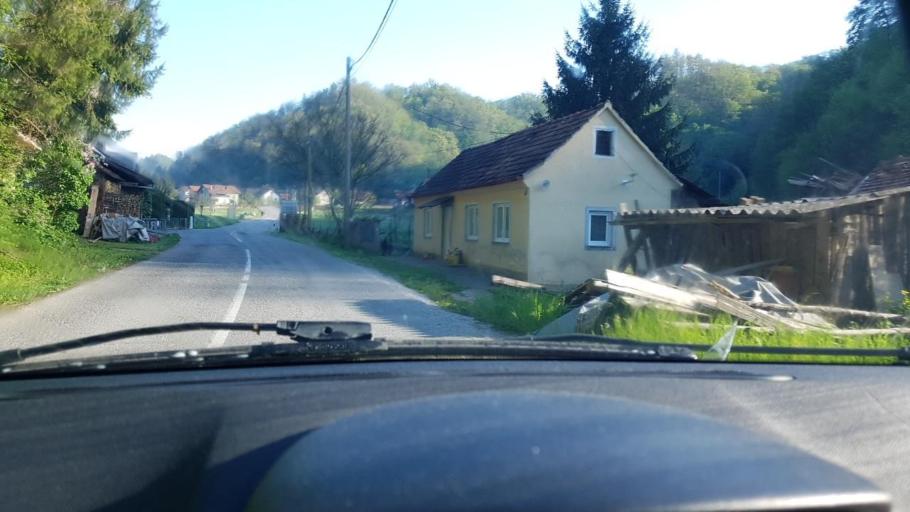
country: HR
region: Krapinsko-Zagorska
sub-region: Grad Krapina
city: Krapina
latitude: 46.2096
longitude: 15.8487
